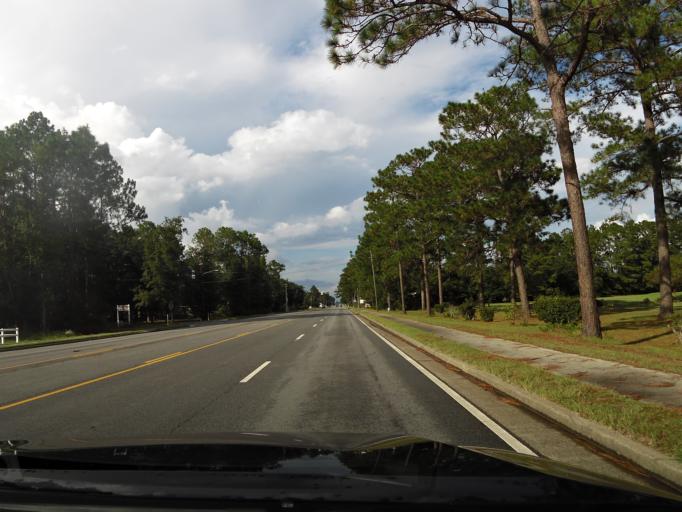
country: US
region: Georgia
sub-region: Liberty County
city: Walthourville
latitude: 31.8044
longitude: -81.6044
